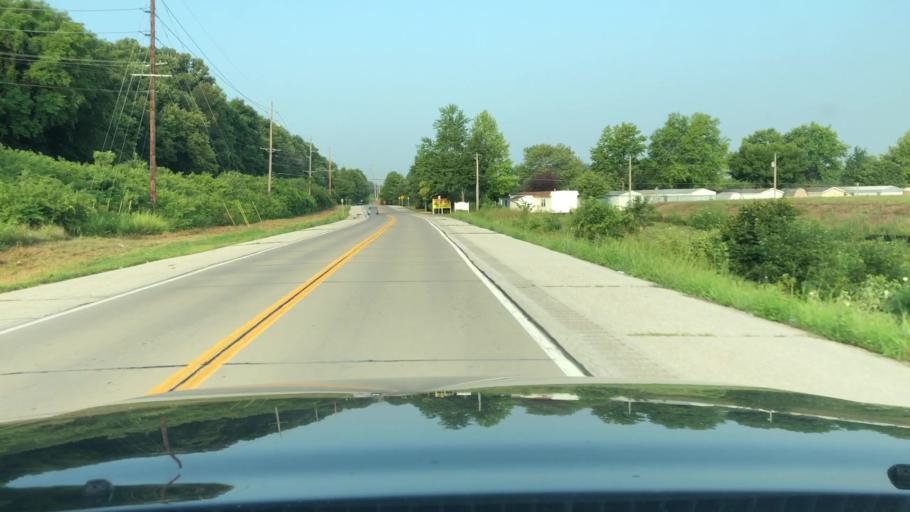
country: US
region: Missouri
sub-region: Saint Charles County
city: Saint Charles
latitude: 38.8163
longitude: -90.5190
